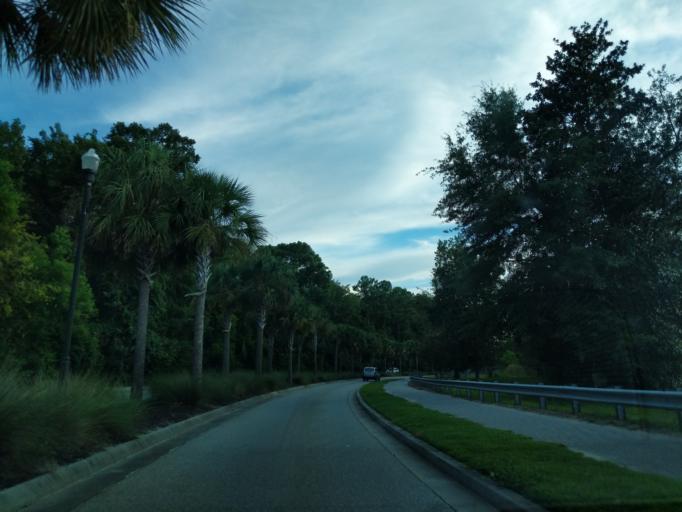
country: US
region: South Carolina
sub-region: Charleston County
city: Isle of Palms
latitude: 32.8348
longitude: -79.8181
